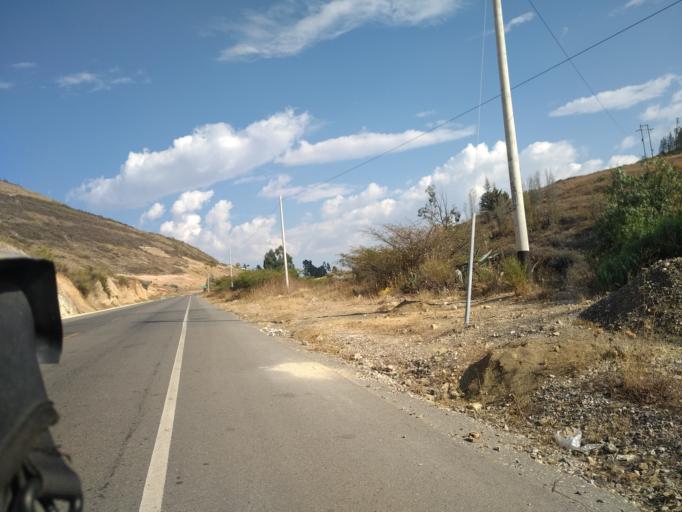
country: PE
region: Cajamarca
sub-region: San Marcos
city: San Marcos
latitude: -7.3775
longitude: -78.1274
